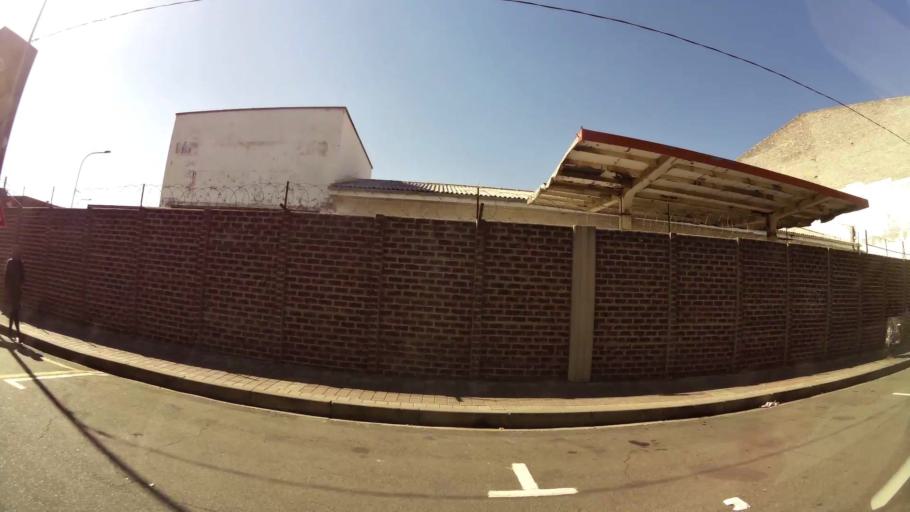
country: ZA
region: Gauteng
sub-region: City of Johannesburg Metropolitan Municipality
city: Johannesburg
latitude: -26.2003
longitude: 28.0606
